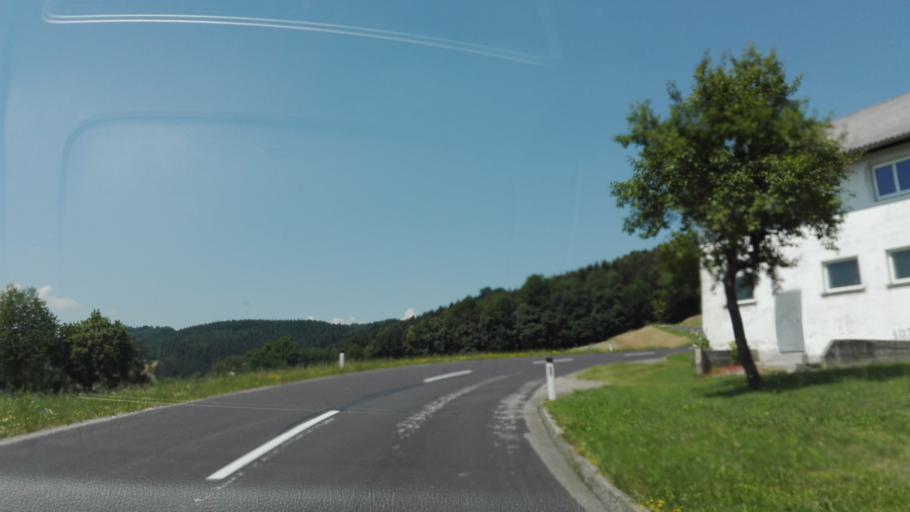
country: AT
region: Upper Austria
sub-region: Politischer Bezirk Grieskirchen
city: Grieskirchen
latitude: 48.3641
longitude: 13.8714
